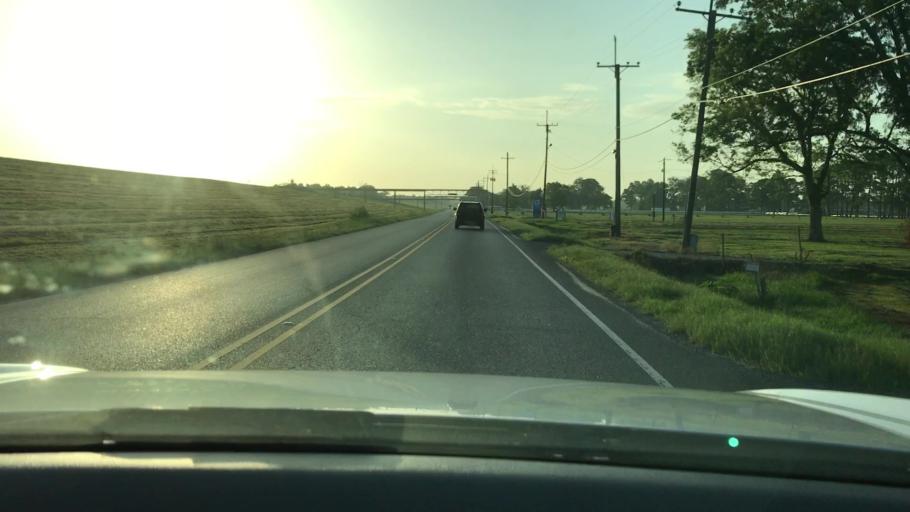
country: US
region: Louisiana
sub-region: Iberville Parish
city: Plaquemine
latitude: 30.2727
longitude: -91.1861
